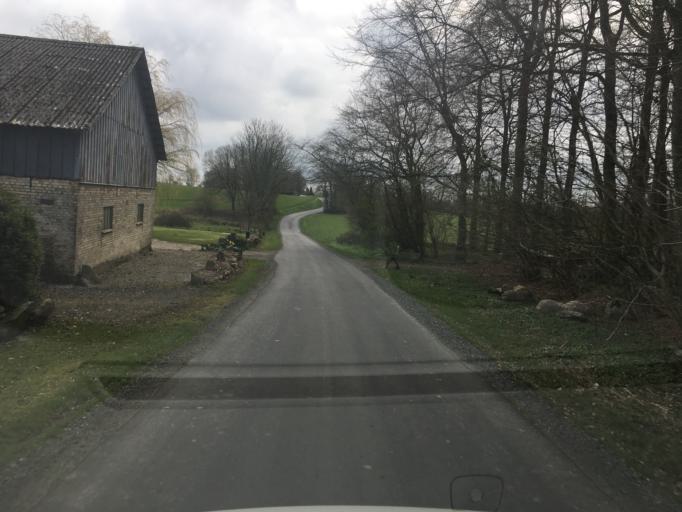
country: DE
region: Schleswig-Holstein
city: Glucksburg
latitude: 54.9050
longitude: 9.5178
